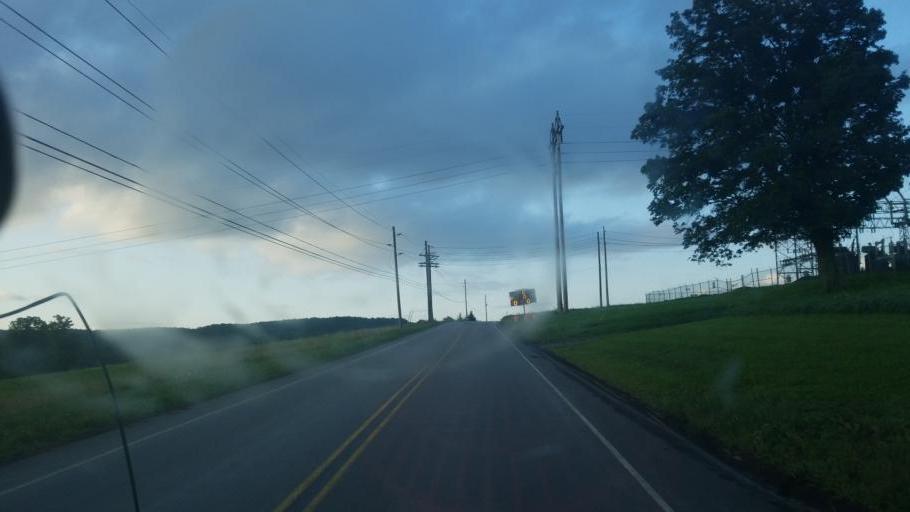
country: US
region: Pennsylvania
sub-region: Potter County
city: Galeton
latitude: 41.8664
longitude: -77.7659
